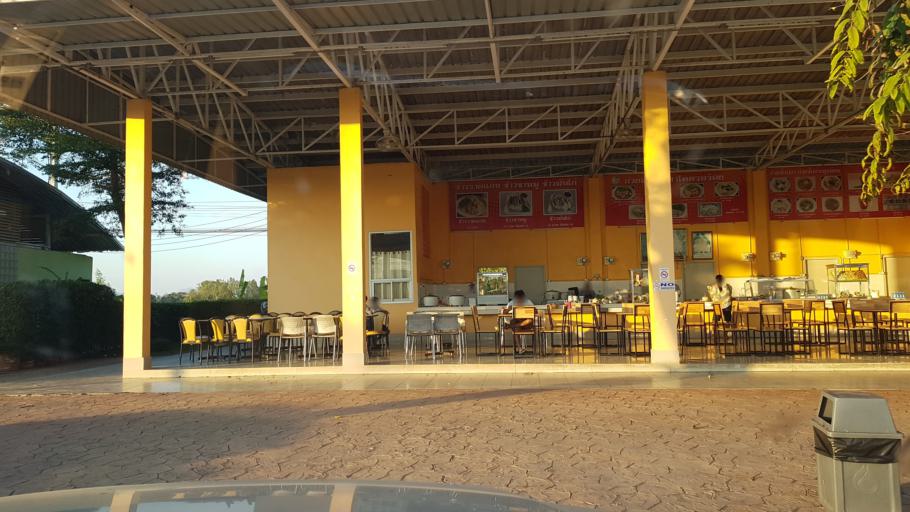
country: TH
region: Khon Kaen
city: Chum Phae
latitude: 16.5846
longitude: 102.0123
